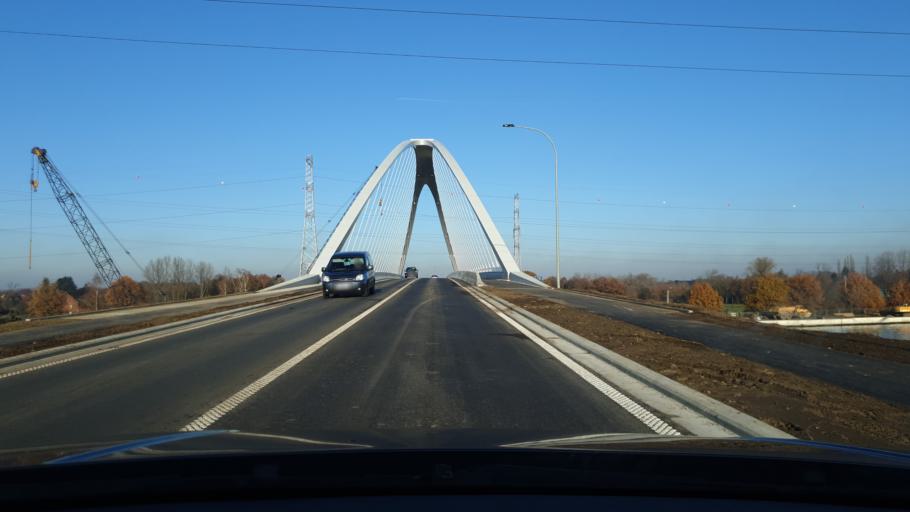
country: BE
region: Flanders
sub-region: Provincie Antwerpen
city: Geel
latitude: 51.1244
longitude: 4.9820
